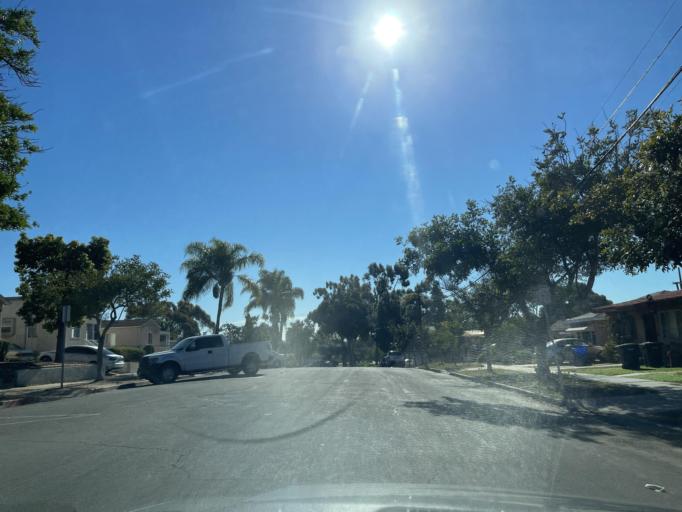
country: US
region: California
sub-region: San Diego County
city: National City
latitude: 32.6743
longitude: -117.1029
